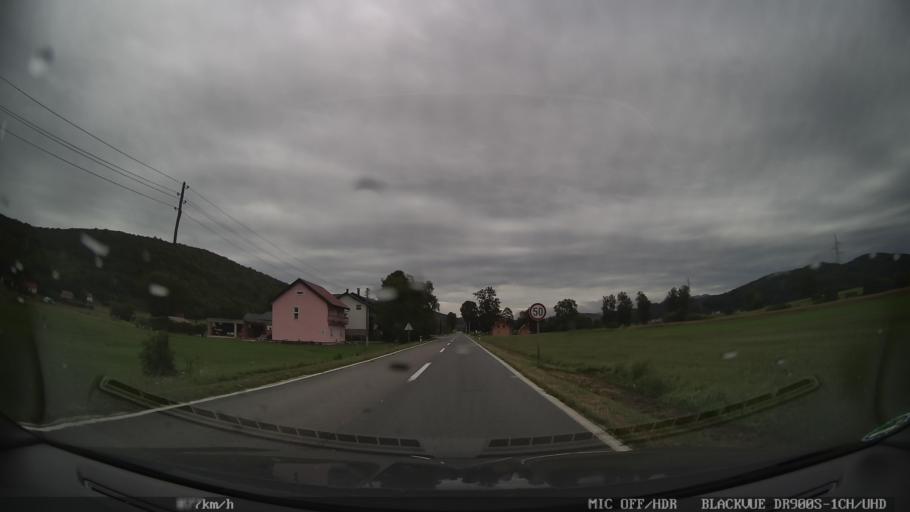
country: HR
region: Licko-Senjska
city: Brinje
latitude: 44.9174
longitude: 15.1538
